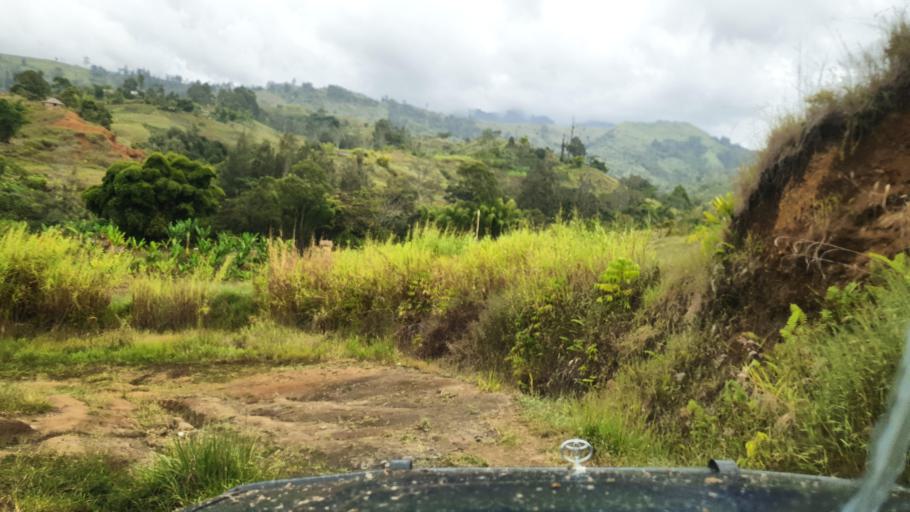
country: PG
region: Jiwaka
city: Minj
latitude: -5.9517
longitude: 144.7745
